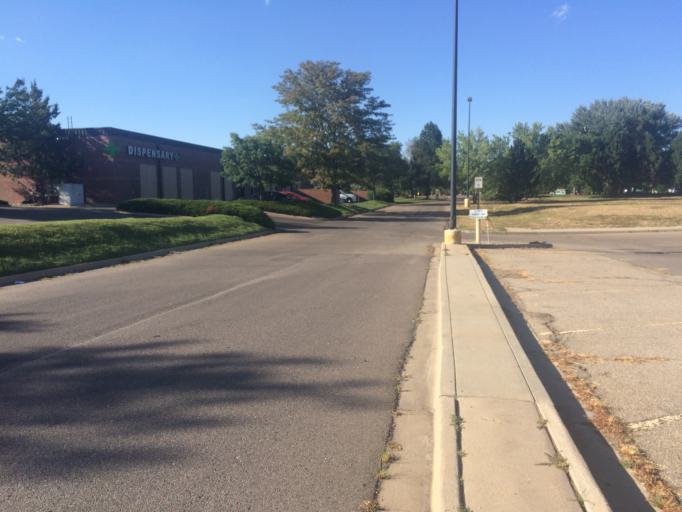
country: US
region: Colorado
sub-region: Boulder County
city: Longmont
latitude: 40.1510
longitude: -105.1298
